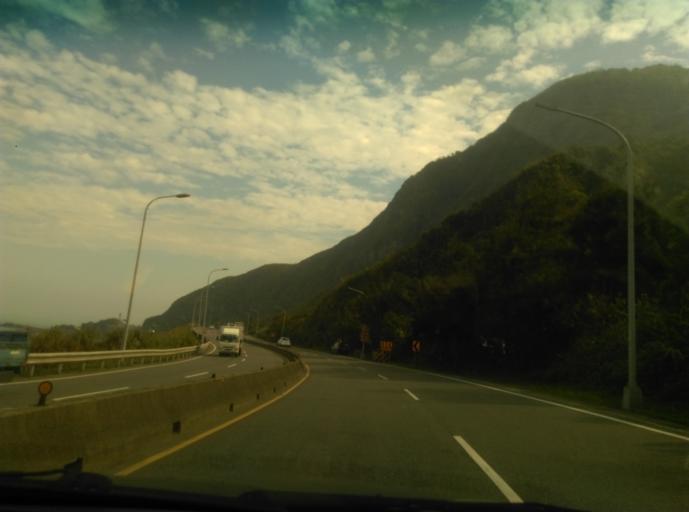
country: TW
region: Taiwan
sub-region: Keelung
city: Keelung
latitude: 25.1766
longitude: 121.7025
